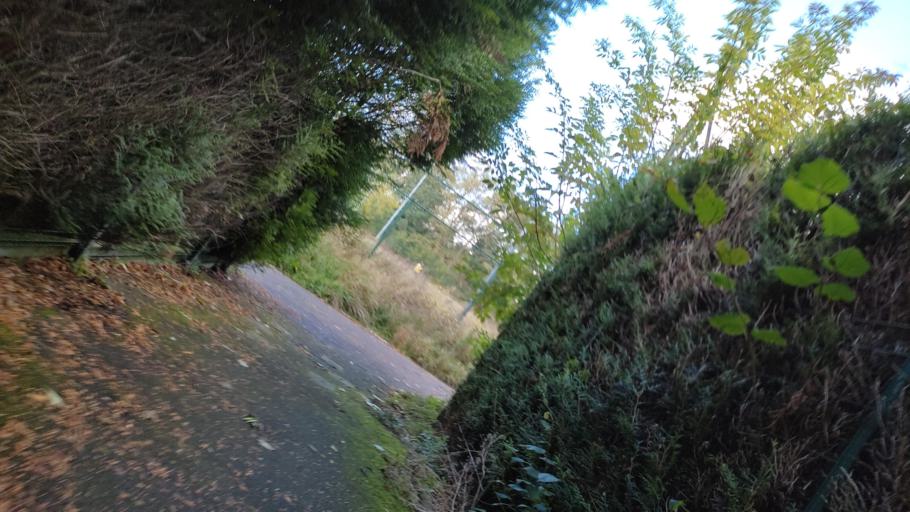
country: FR
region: Nord-Pas-de-Calais
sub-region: Departement du Pas-de-Calais
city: Saint-Nicolas
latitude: 50.3075
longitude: 2.7940
